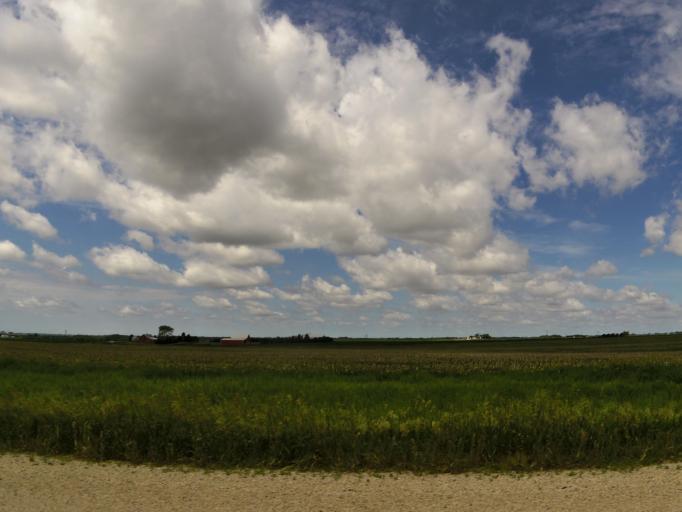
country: US
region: Iowa
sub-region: Chickasaw County
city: New Hampton
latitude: 43.1291
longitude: -92.2981
